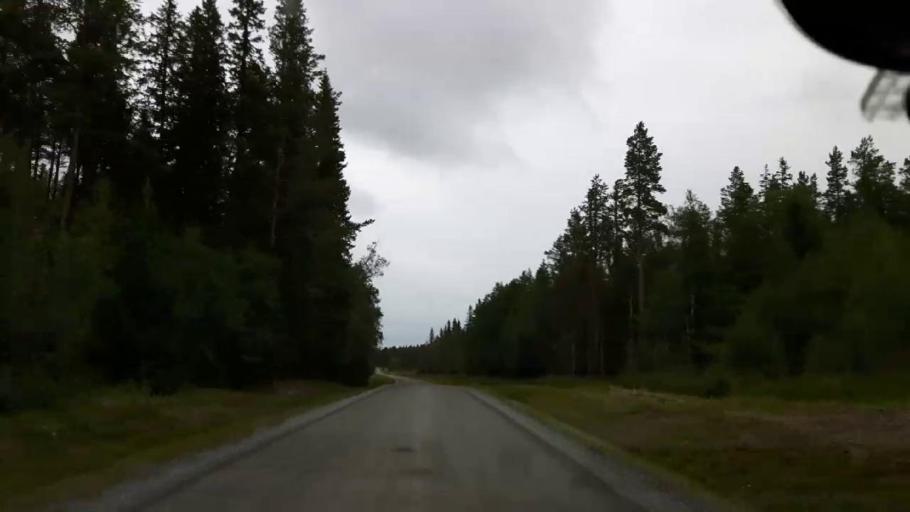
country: SE
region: Jaemtland
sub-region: OEstersunds Kommun
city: Ostersund
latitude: 63.1109
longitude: 14.5453
